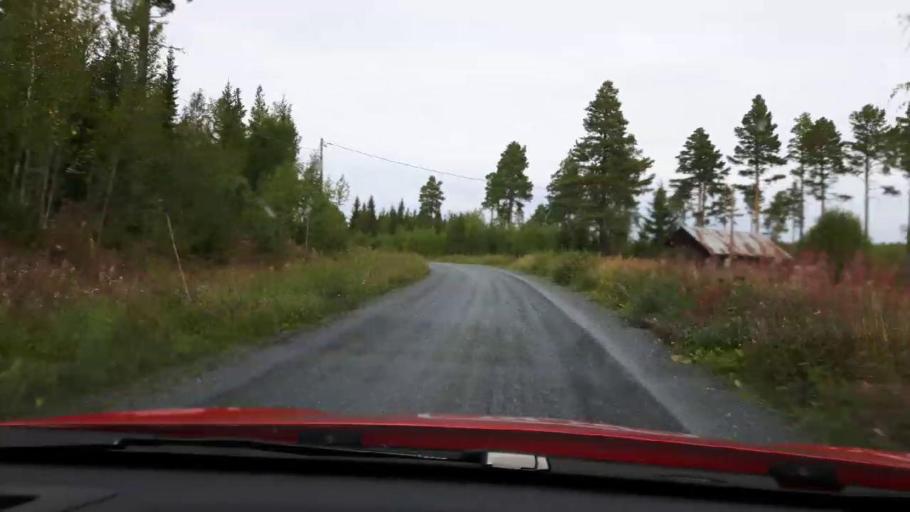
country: SE
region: Jaemtland
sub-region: Are Kommun
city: Jarpen
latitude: 63.2795
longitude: 13.7324
